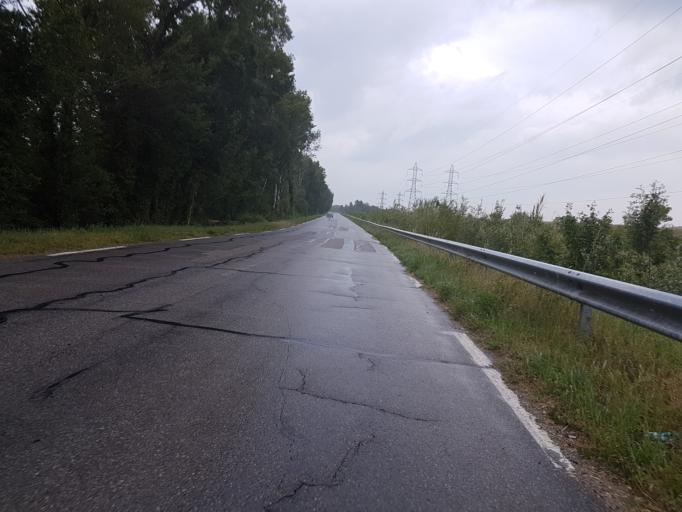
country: FR
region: Languedoc-Roussillon
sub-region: Departement du Gard
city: Villeneuve-les-Avignon
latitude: 43.9844
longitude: 4.8212
